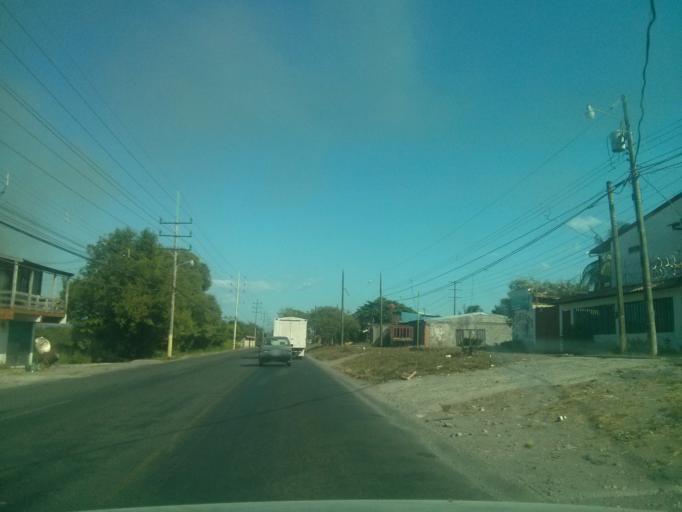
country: CR
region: Puntarenas
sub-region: Canton Central de Puntarenas
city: Chacarita
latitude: 9.9805
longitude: -84.7806
